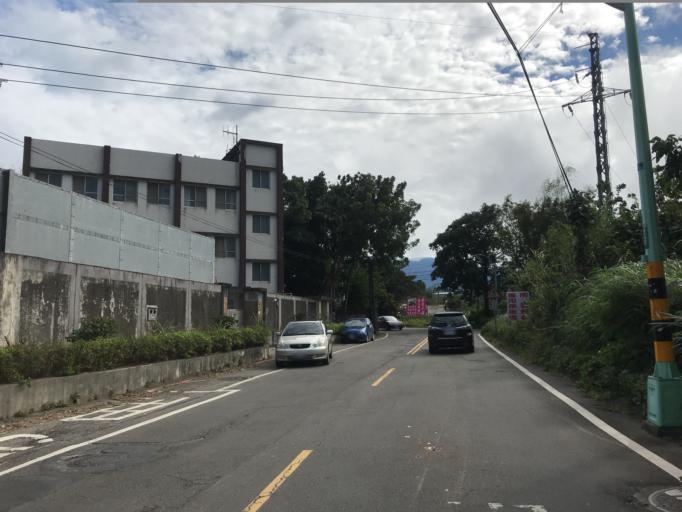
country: TW
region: Taiwan
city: Daxi
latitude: 24.8440
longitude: 121.2392
